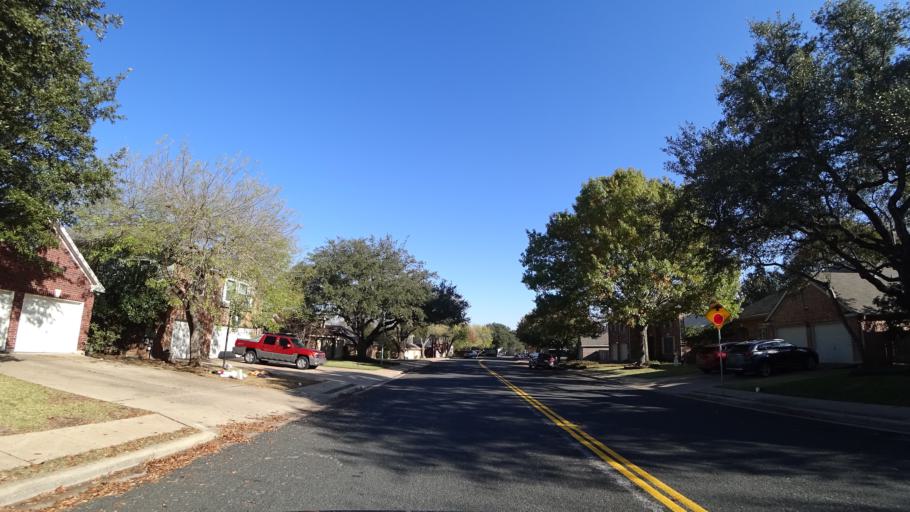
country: US
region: Texas
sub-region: Williamson County
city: Brushy Creek
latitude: 30.4897
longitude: -97.7418
